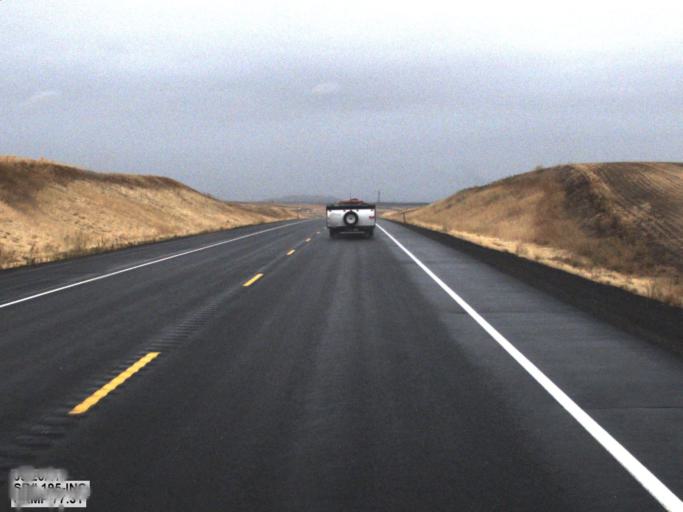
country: US
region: Washington
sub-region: Spokane County
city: Cheney
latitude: 47.4016
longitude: -117.3915
